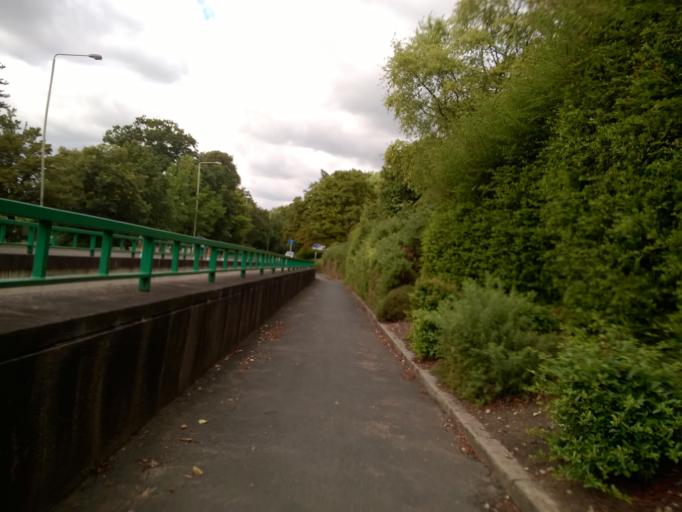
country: GB
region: England
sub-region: Leicestershire
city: Glenfield
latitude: 52.6555
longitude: -1.1899
